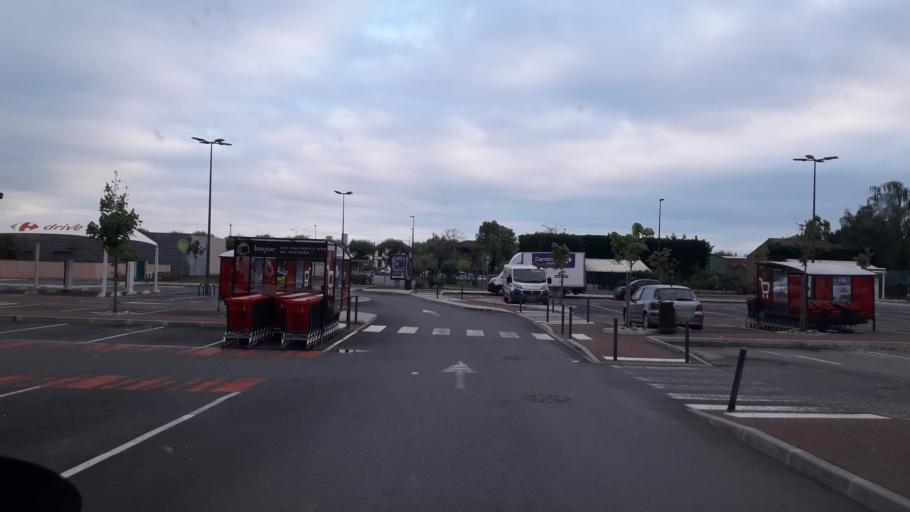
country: FR
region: Midi-Pyrenees
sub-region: Departement de la Haute-Garonne
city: Cazeres
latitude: 43.2104
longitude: 1.0843
